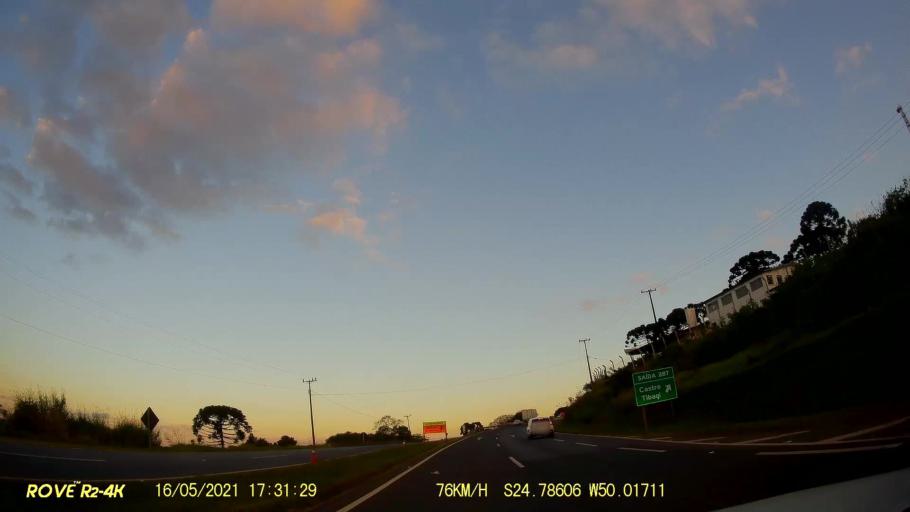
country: BR
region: Parana
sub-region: Castro
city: Castro
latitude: -24.7862
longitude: -50.0170
